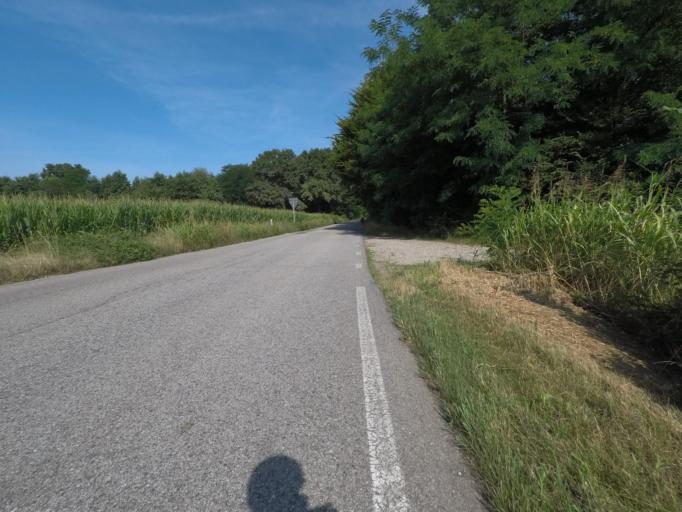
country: IT
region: Friuli Venezia Giulia
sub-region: Provincia di Udine
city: Colloredo di Prato
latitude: 46.0584
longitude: 13.1144
